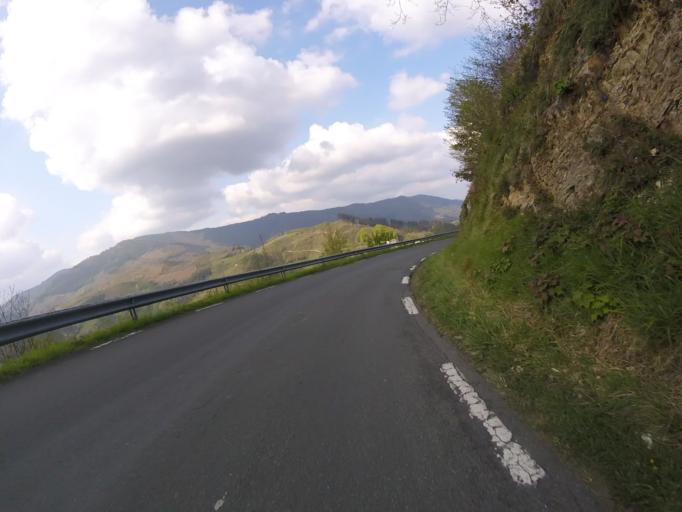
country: ES
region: Basque Country
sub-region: Provincia de Guipuzcoa
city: Azkoitia
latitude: 43.2052
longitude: -2.3538
